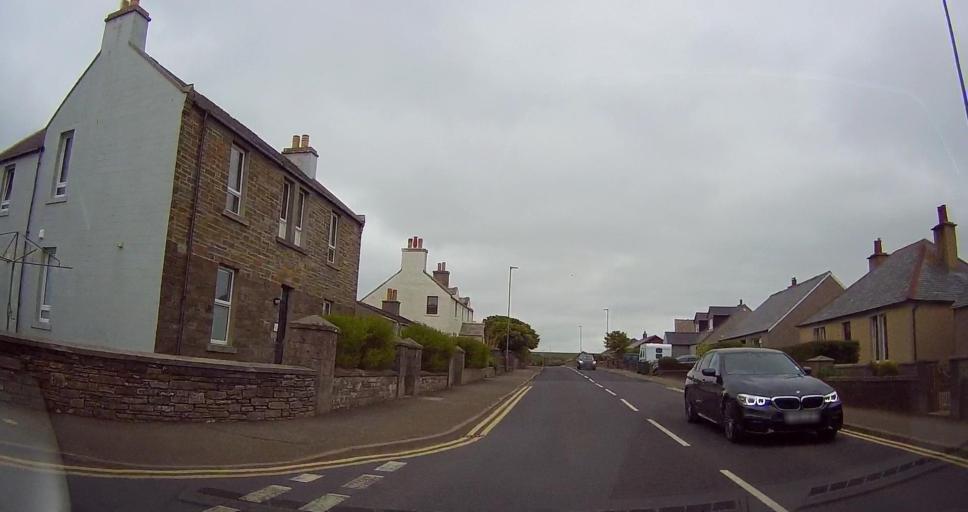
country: GB
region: Scotland
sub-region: Orkney Islands
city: Kirkwall
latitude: 58.9753
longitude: -2.9530
